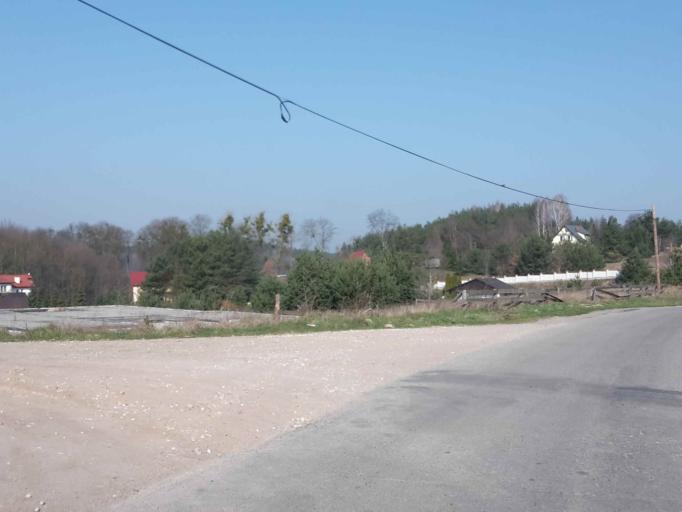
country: PL
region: Kujawsko-Pomorskie
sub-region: Powiat brodnicki
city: Brodnica
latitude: 53.3365
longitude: 19.3563
